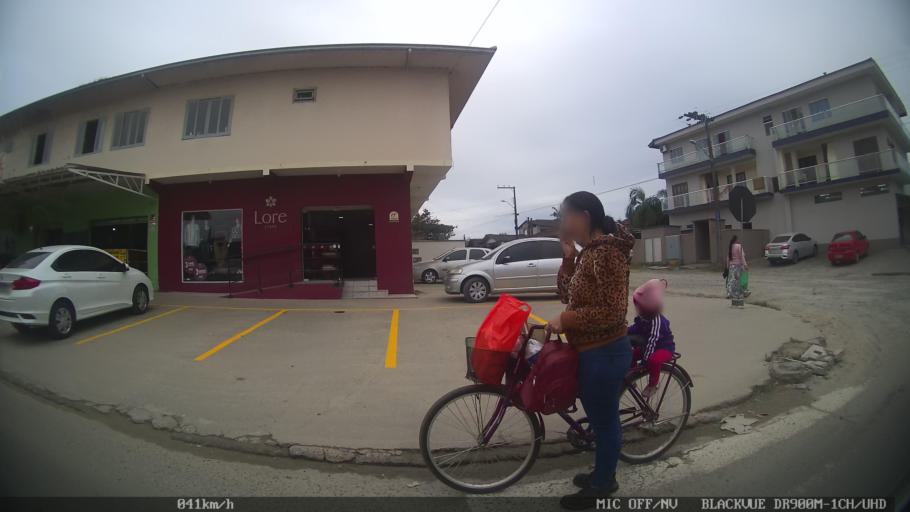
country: BR
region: Santa Catarina
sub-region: Joinville
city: Joinville
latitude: -26.3298
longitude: -48.9073
